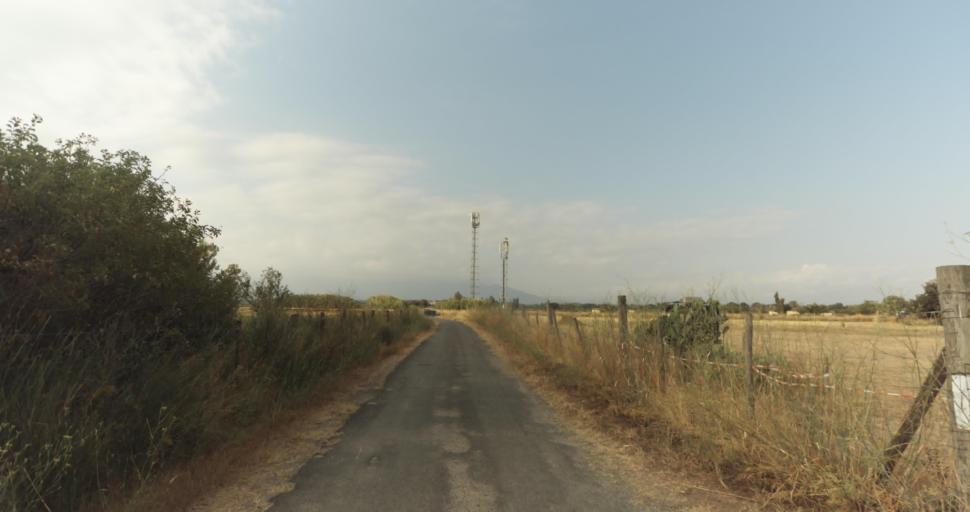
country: FR
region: Languedoc-Roussillon
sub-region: Departement des Pyrenees-Orientales
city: Villeneuve-de-la-Raho
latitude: 42.6268
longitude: 2.9310
